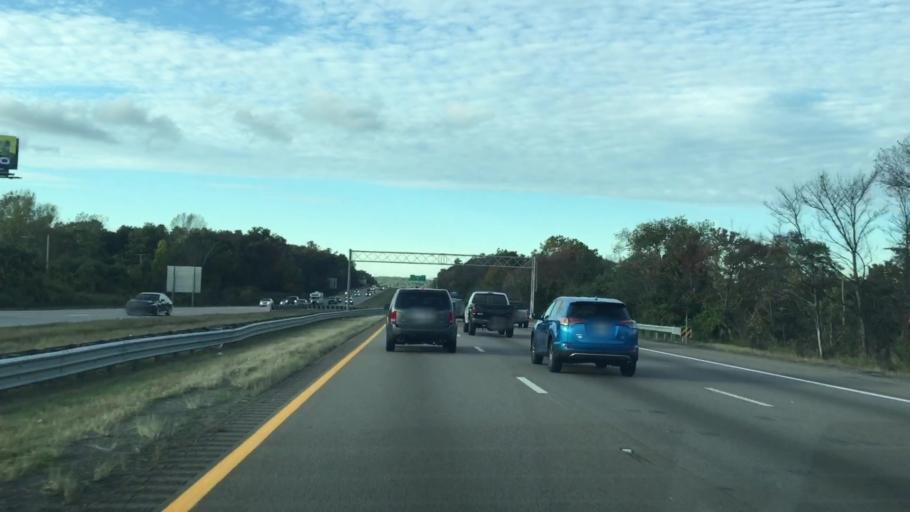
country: US
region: Massachusetts
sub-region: Norfolk County
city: Randolph
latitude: 42.1786
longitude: -71.0753
